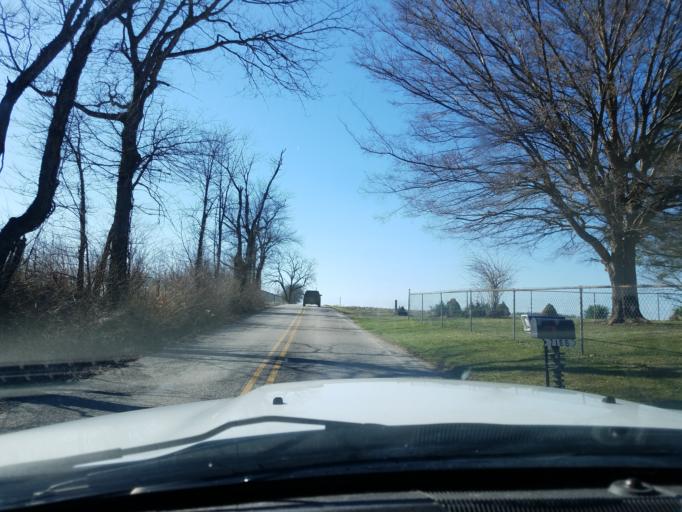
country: US
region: Indiana
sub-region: Johnson County
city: Franklin
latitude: 39.4955
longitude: -85.9672
